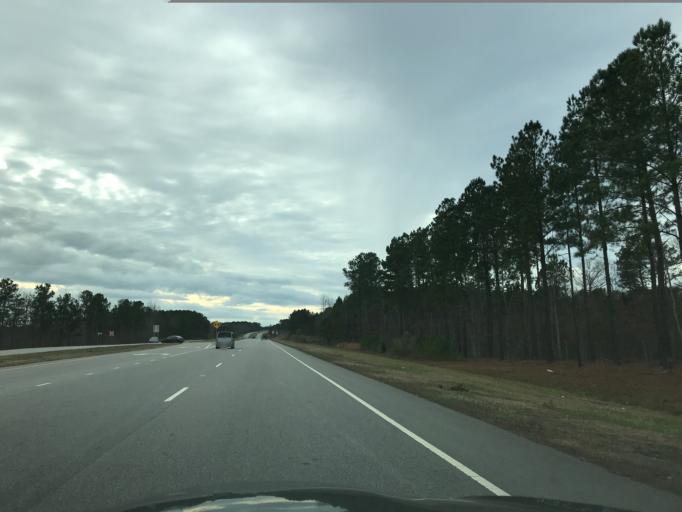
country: US
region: North Carolina
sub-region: Wake County
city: Rolesville
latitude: 35.9278
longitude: -78.4373
